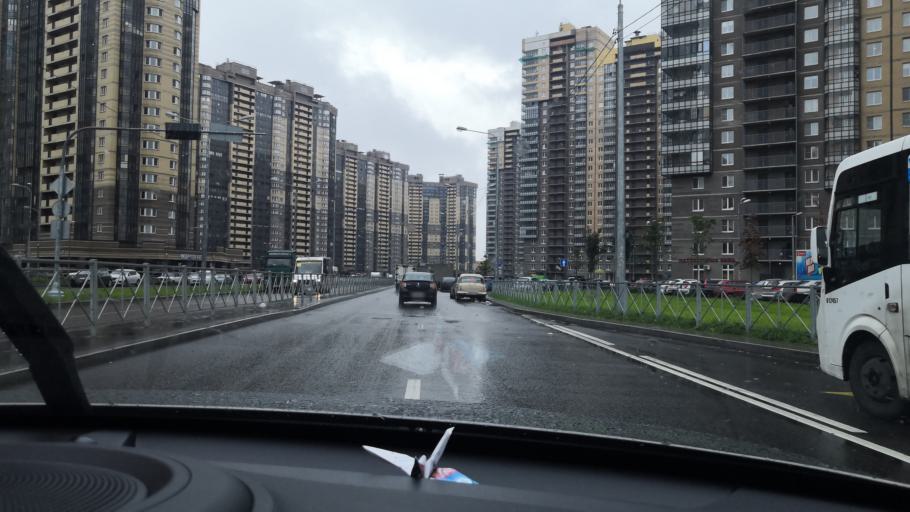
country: RU
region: Leningrad
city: Parnas
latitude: 60.0822
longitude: 30.3416
